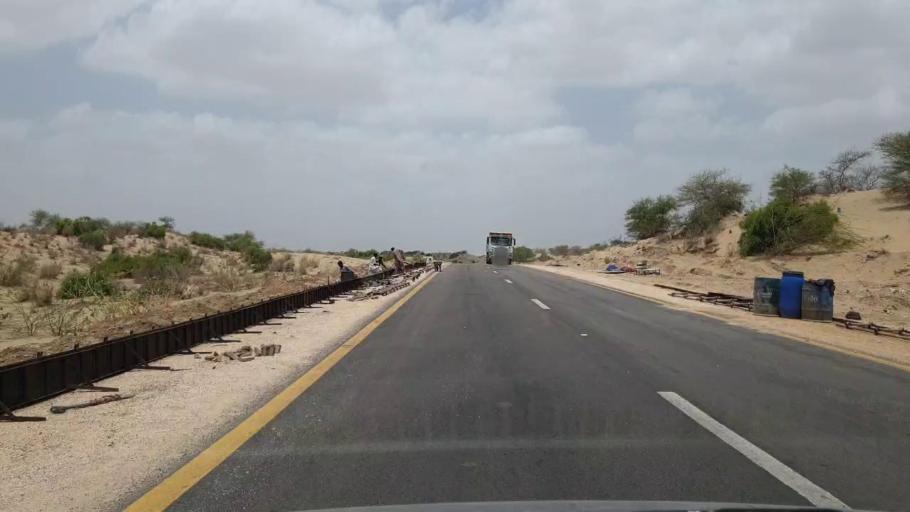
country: PK
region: Sindh
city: Naukot
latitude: 24.8426
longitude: 69.5602
